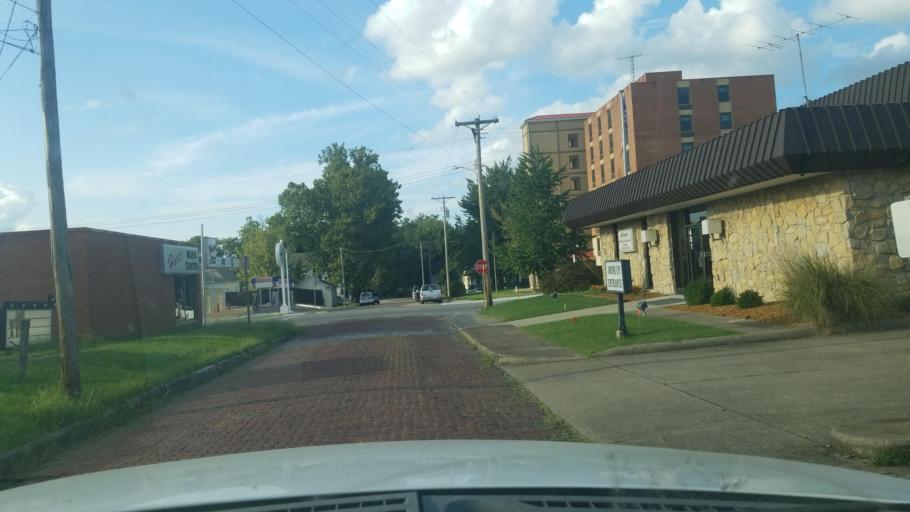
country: US
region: Illinois
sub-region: Saline County
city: Harrisburg
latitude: 37.7372
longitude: -88.5362
